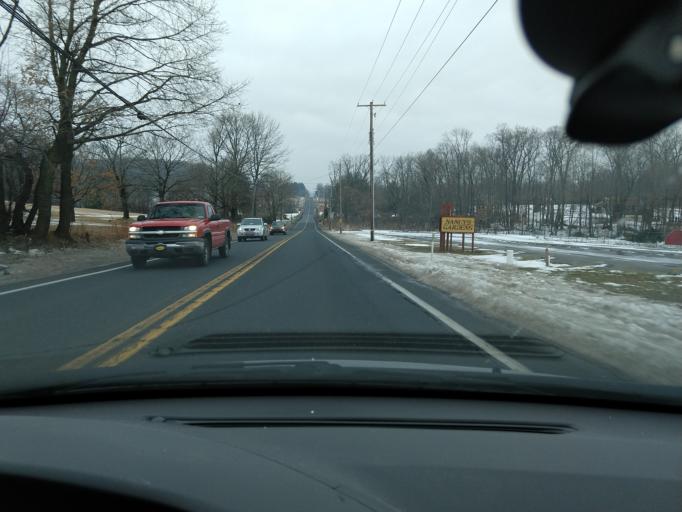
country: US
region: Pennsylvania
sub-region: Lehigh County
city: Macungie
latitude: 40.4775
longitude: -75.5300
